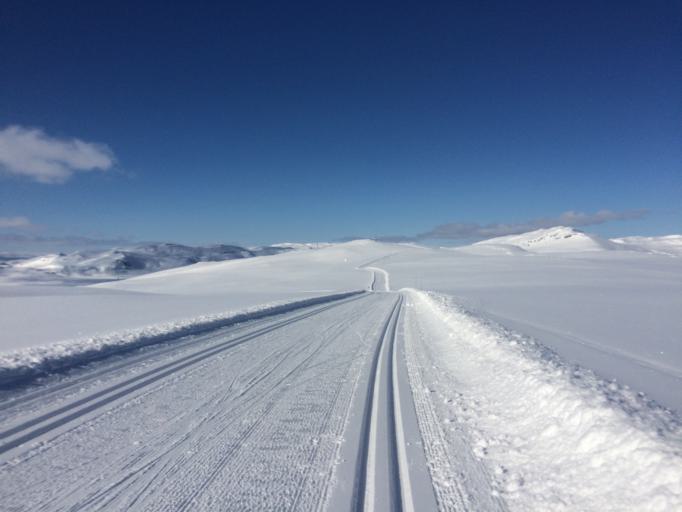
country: NO
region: Oppland
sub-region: Ringebu
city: Ringebu
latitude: 61.3572
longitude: 10.0858
